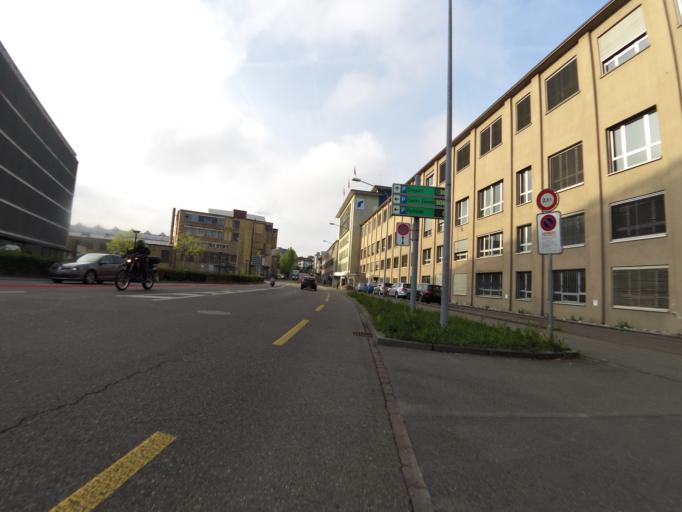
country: CH
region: Zurich
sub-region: Bezirk Zuerich
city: Zuerich (Kreis 11) / Oerlikon
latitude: 47.4127
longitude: 8.5377
